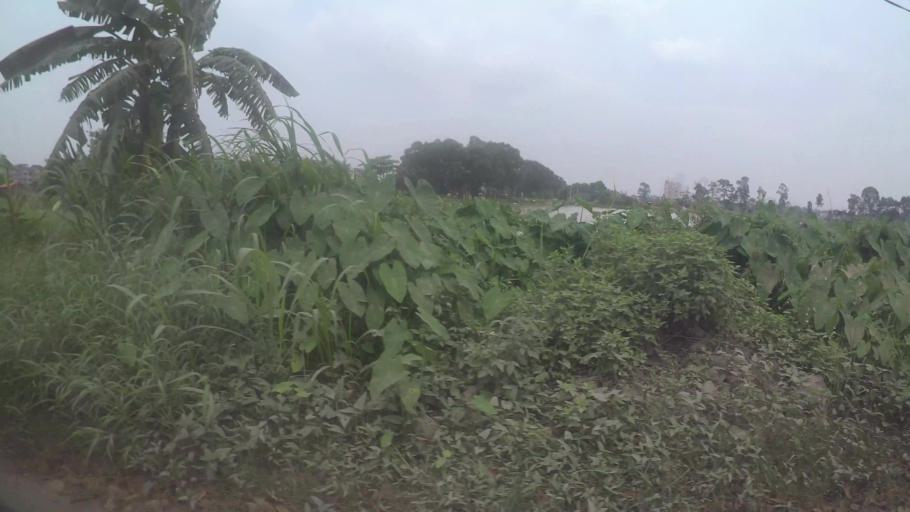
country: VN
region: Ha Noi
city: Cau Dien
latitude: 21.0222
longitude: 105.7431
